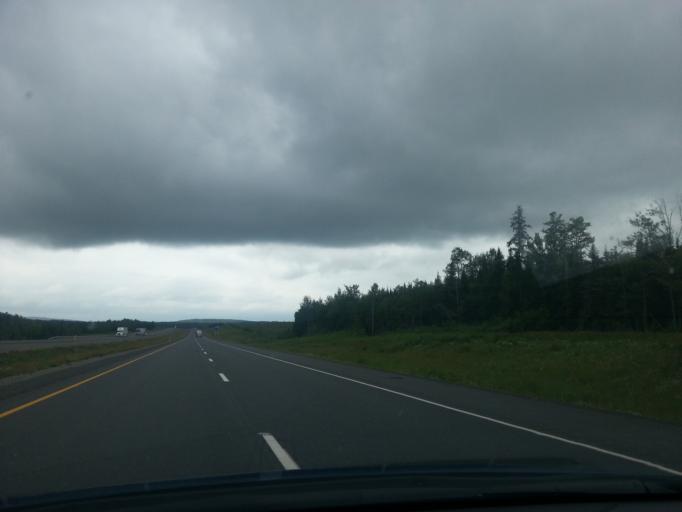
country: US
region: Maine
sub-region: Aroostook County
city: Limestone
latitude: 46.9113
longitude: -67.7359
